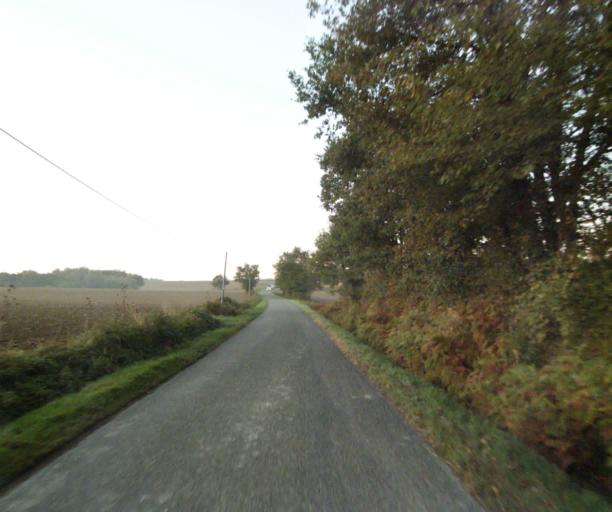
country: FR
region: Midi-Pyrenees
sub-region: Departement du Gers
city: Vic-Fezensac
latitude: 43.7827
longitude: 0.2223
